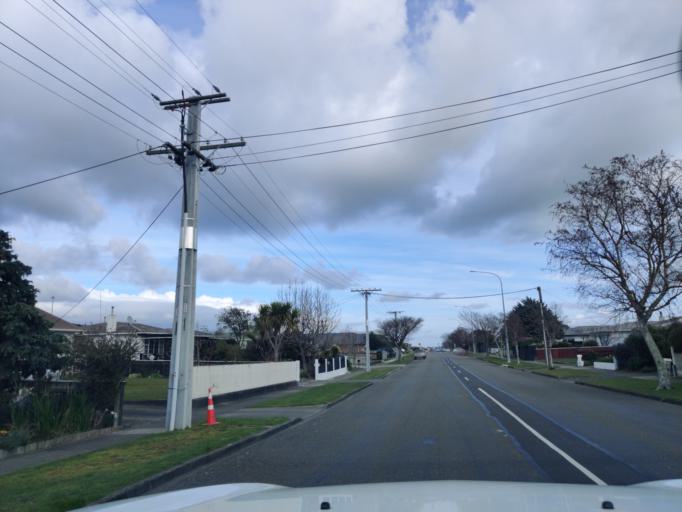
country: NZ
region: Manawatu-Wanganui
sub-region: Palmerston North City
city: Palmerston North
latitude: -40.3353
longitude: 175.6087
